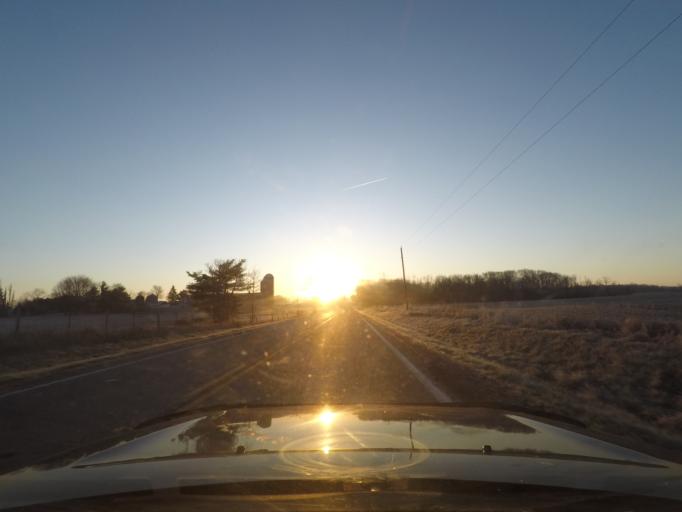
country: US
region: Indiana
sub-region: Saint Joseph County
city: North Liberty
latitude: 41.4483
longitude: -86.3908
